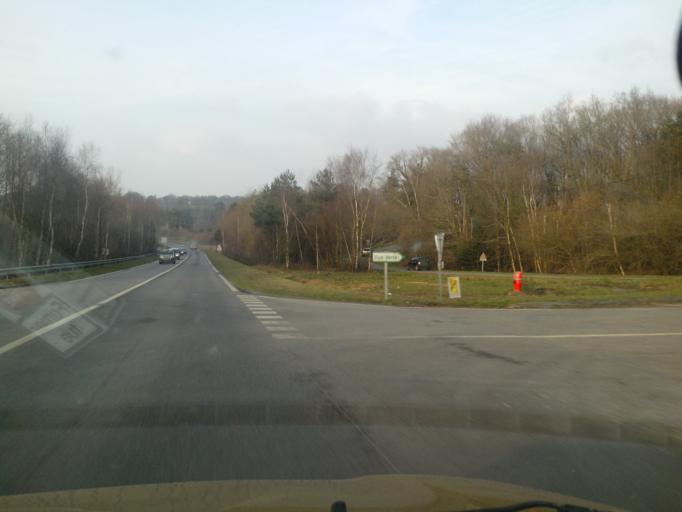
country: FR
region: Brittany
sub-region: Departement du Morbihan
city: Molac
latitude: 47.7153
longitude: -2.4409
